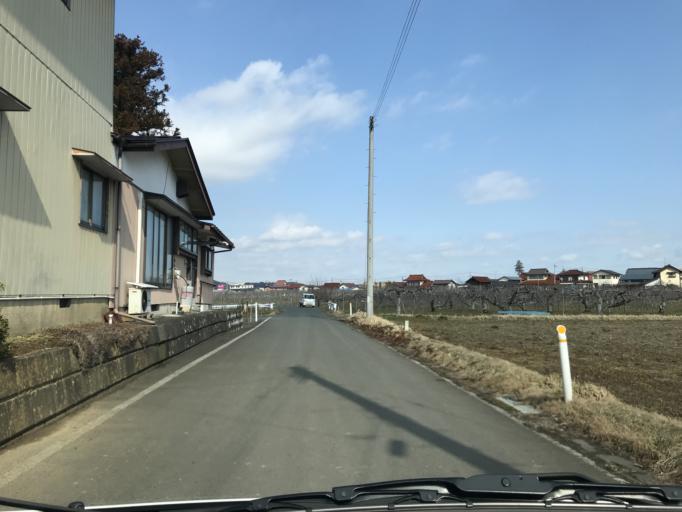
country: JP
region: Iwate
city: Mizusawa
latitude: 39.0409
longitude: 141.1389
